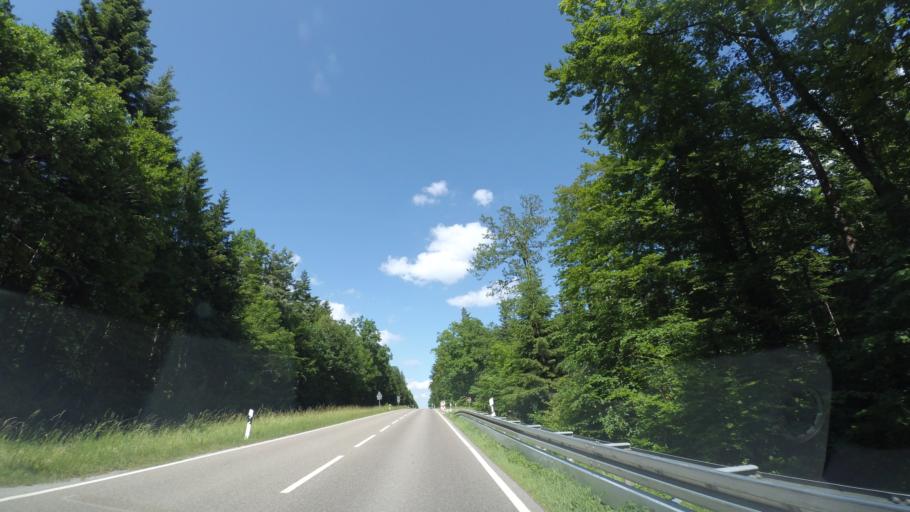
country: DE
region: Baden-Wuerttemberg
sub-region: Regierungsbezirk Stuttgart
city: Gaildorf
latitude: 49.0147
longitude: 9.7956
